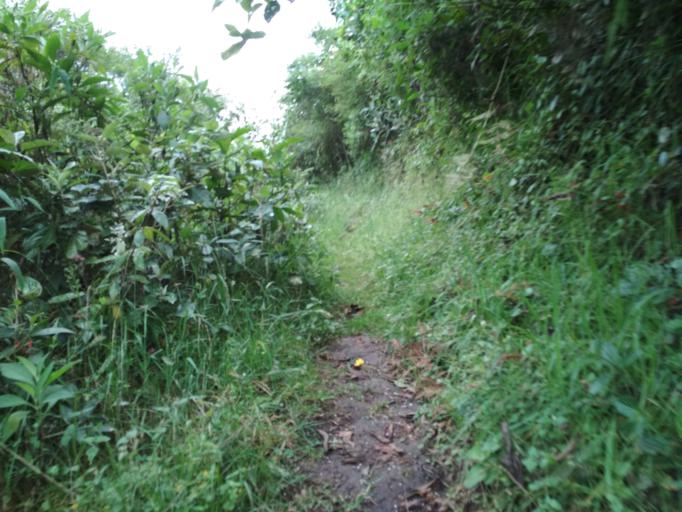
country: CO
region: Cauca
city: Jambalo
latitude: 2.7384
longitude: -76.3454
